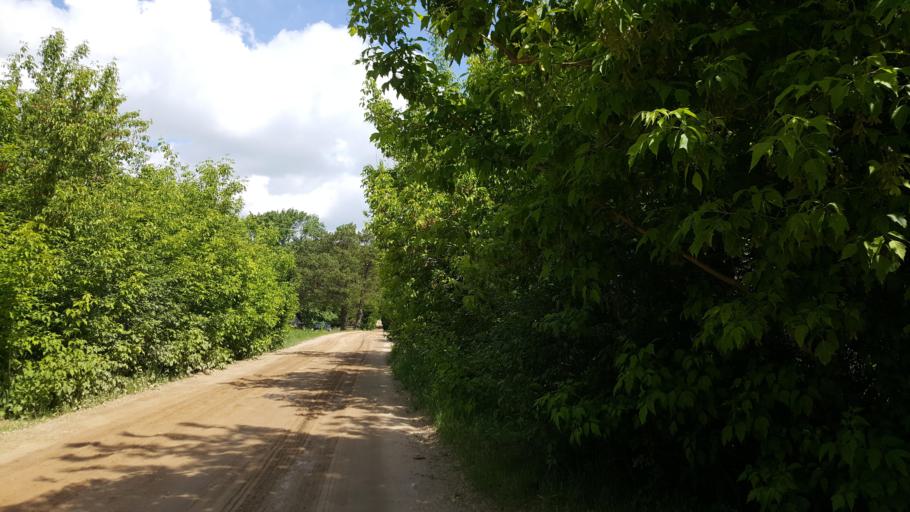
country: BY
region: Brest
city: Kamyanyets
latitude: 52.3908
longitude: 23.8843
